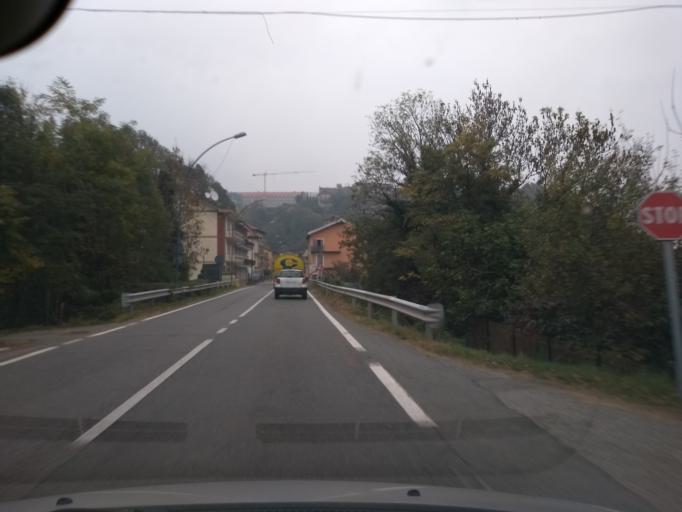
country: IT
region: Piedmont
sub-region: Provincia di Torino
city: Germagnano
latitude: 45.2672
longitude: 7.4751
